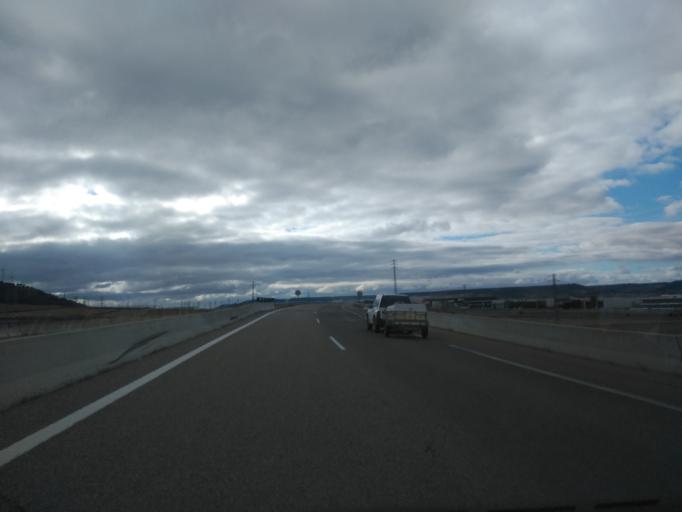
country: ES
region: Castille and Leon
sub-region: Provincia de Palencia
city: Villalobon
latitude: 42.0100
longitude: -4.4975
